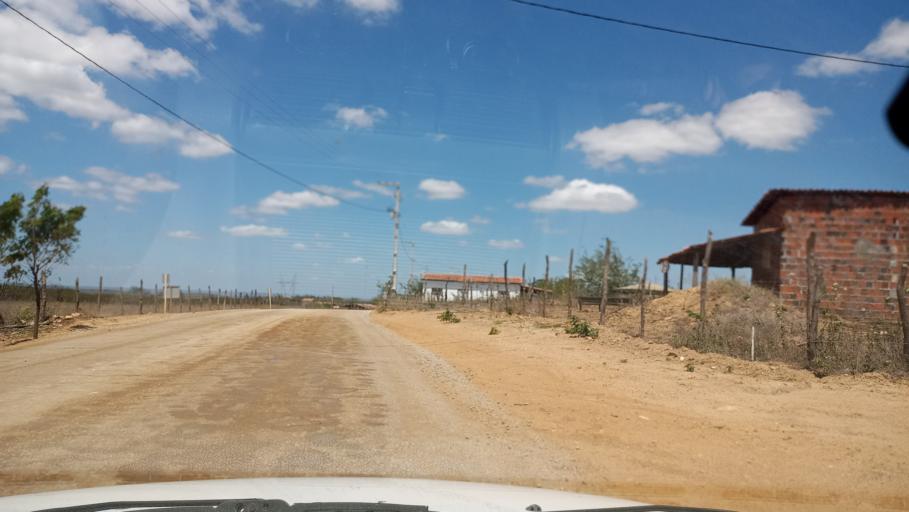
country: BR
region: Rio Grande do Norte
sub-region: Sao Paulo Do Potengi
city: Sao Paulo do Potengi
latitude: -5.7774
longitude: -35.9141
